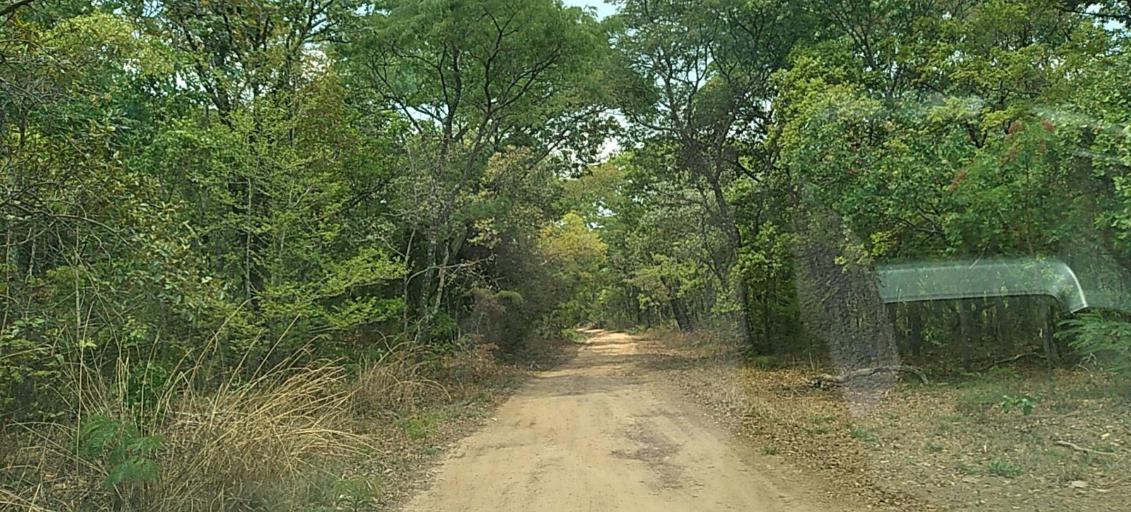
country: ZM
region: Copperbelt
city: Chingola
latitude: -12.7710
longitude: 27.6888
